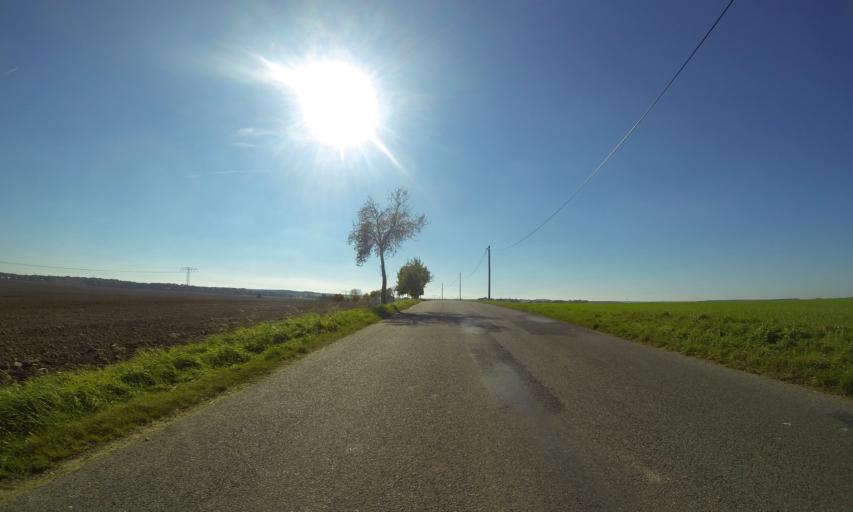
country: DE
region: Saxony
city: Ebersbach
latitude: 51.2378
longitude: 13.5943
